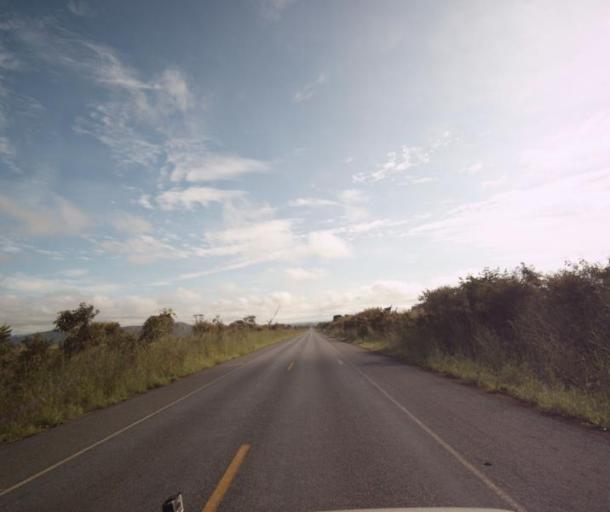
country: BR
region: Goias
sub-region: Pirenopolis
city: Pirenopolis
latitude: -15.5222
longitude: -48.6243
